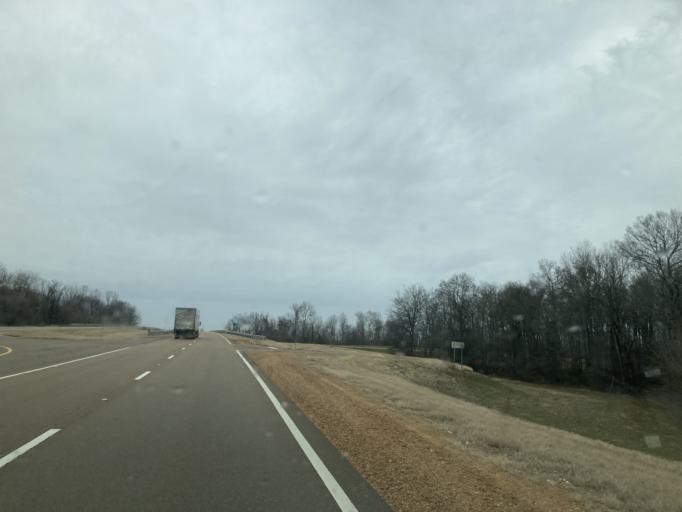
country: US
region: Mississippi
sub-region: Humphreys County
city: Belzoni
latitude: 33.0509
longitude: -90.4677
